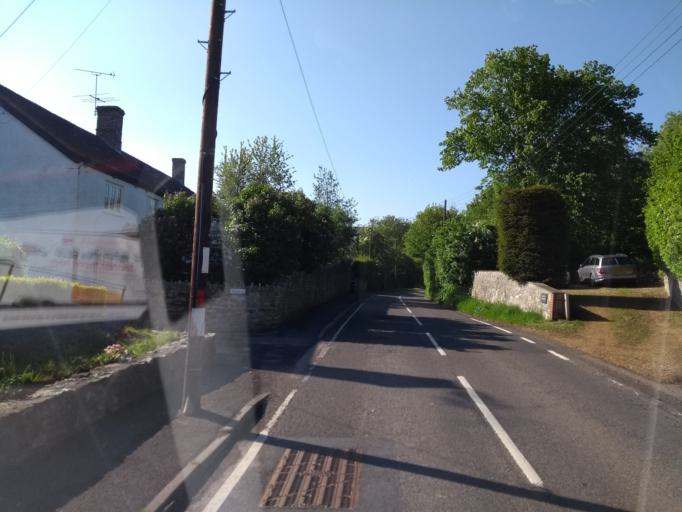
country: GB
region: England
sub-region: Somerset
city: Taunton
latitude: 50.9680
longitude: -3.0944
